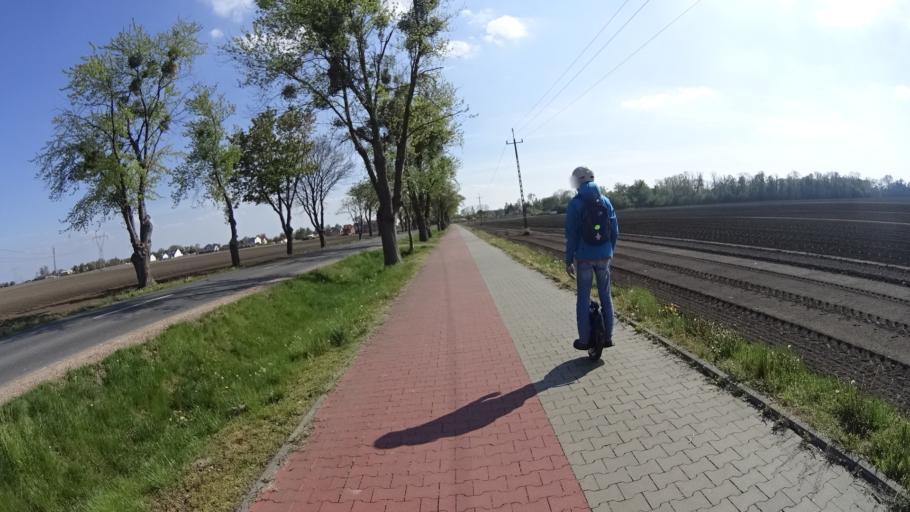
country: PL
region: Masovian Voivodeship
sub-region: Powiat warszawski zachodni
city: Stare Babice
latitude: 52.2372
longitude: 20.8168
